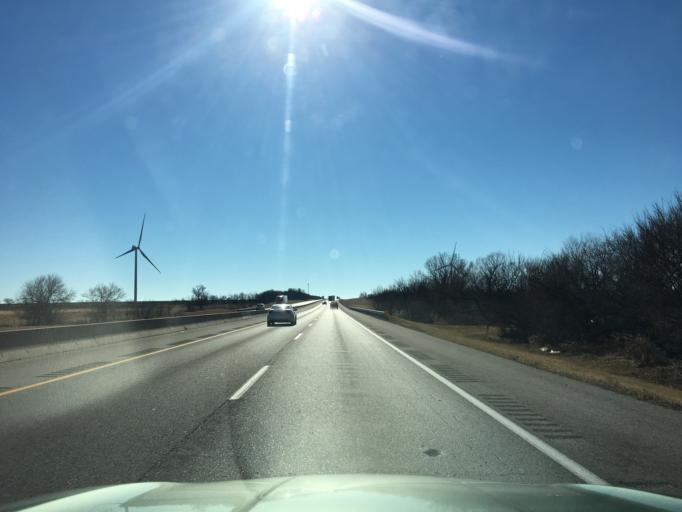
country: US
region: Kansas
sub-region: Sumner County
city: Wellington
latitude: 37.1350
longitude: -97.3391
